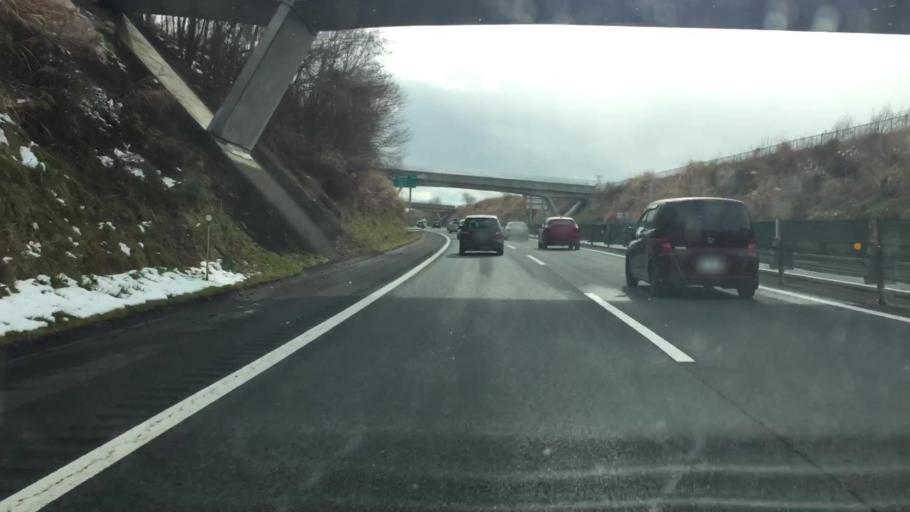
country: JP
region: Gunma
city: Numata
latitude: 36.6282
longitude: 139.0685
